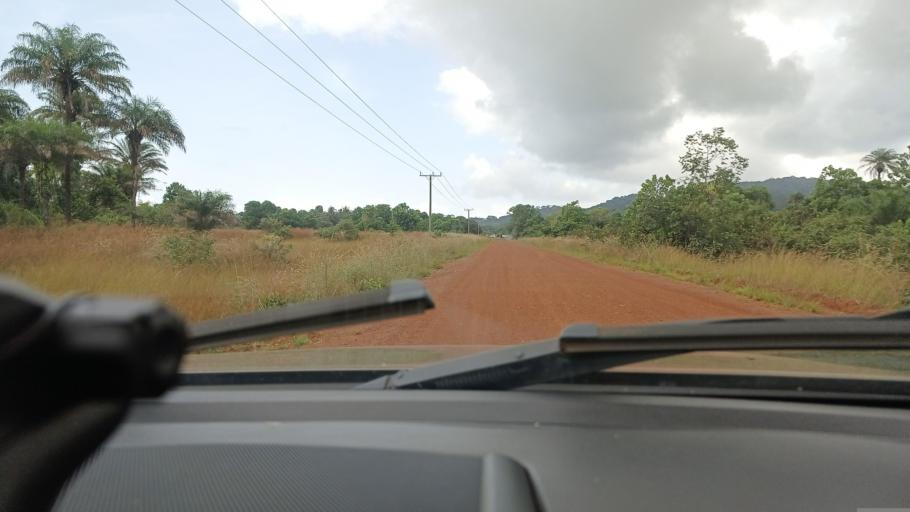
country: LR
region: Grand Cape Mount
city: Robertsport
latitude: 6.7044
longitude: -11.3268
